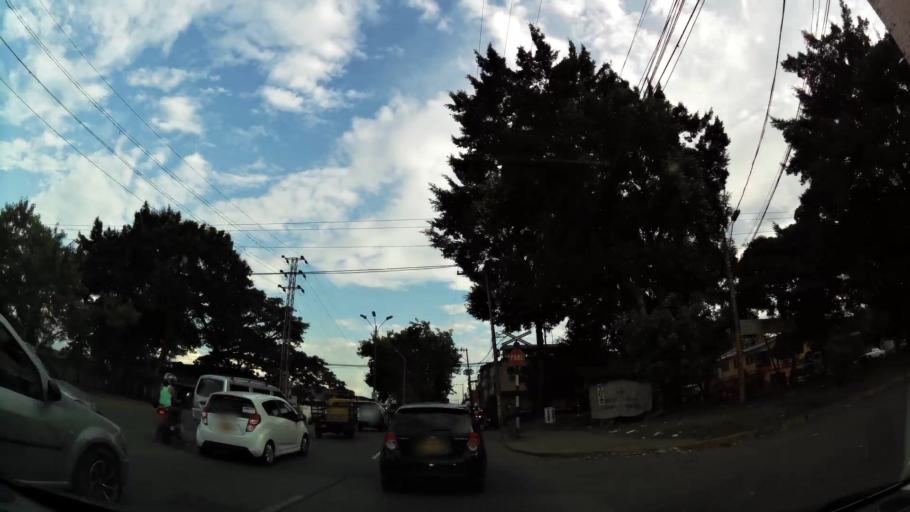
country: CO
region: Valle del Cauca
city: Cali
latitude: 3.4568
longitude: -76.5127
